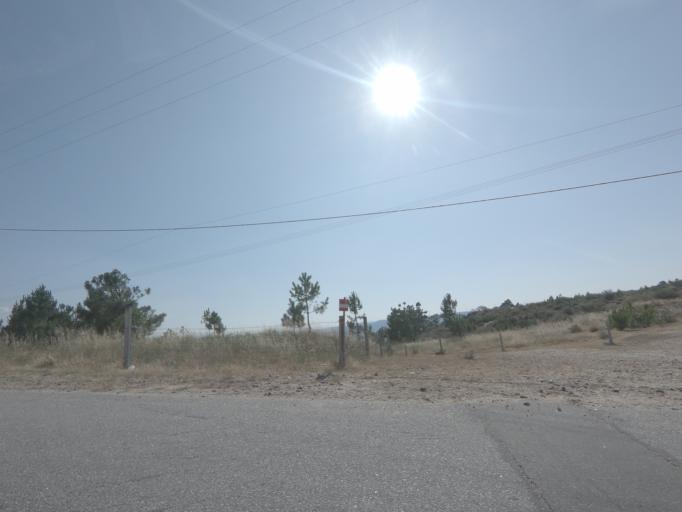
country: PT
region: Viseu
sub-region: Tabuaco
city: Tabuaco
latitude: 41.0442
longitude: -7.5712
